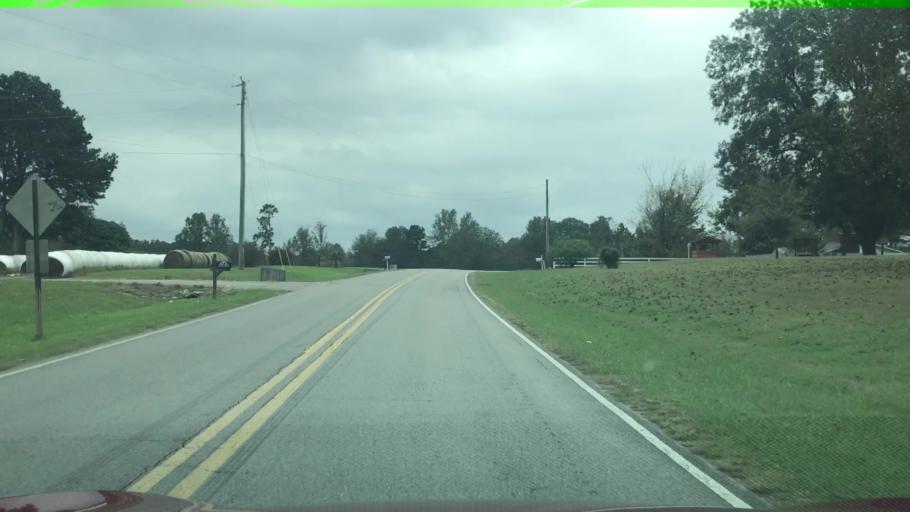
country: US
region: Alabama
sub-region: Cullman County
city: Good Hope
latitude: 34.1089
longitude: -87.0359
